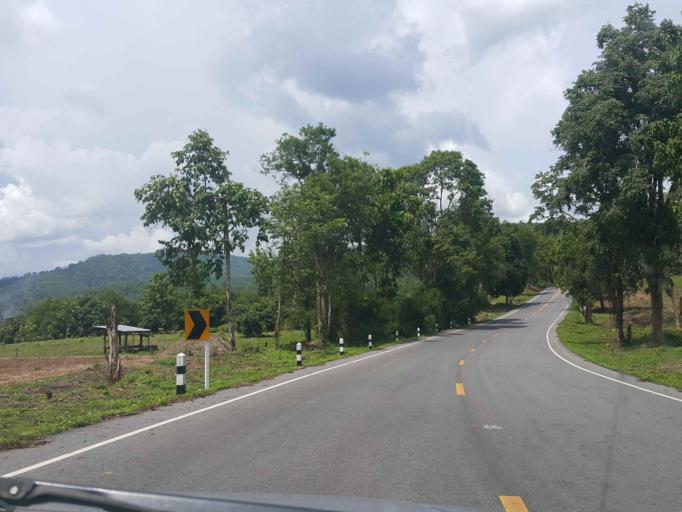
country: TH
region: Nan
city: Ban Luang
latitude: 18.8676
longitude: 100.4685
